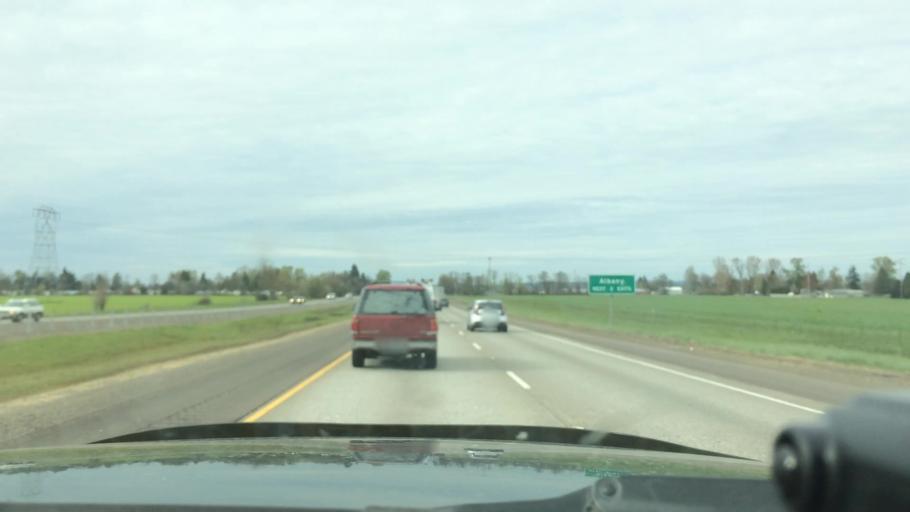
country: US
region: Oregon
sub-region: Linn County
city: Albany
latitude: 44.5997
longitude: -123.0619
